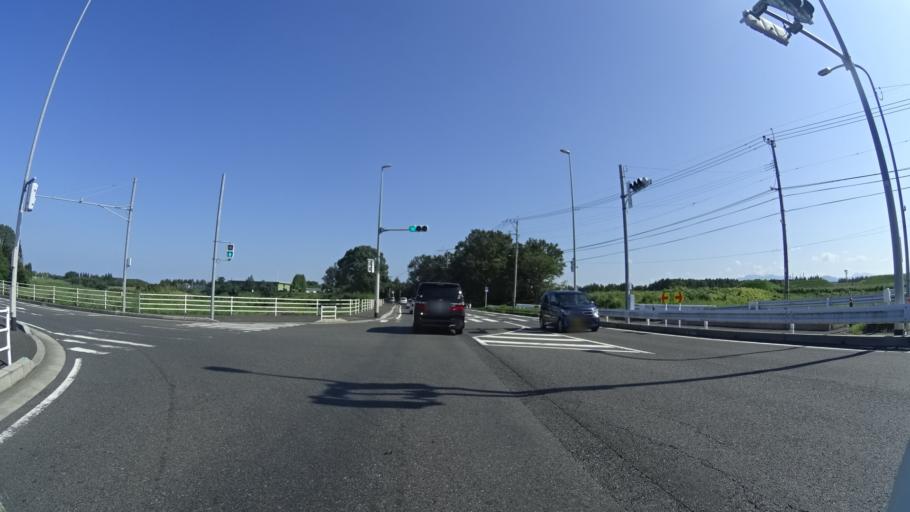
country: JP
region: Fukuoka
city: Tsuiki
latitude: 33.6781
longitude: 131.0055
